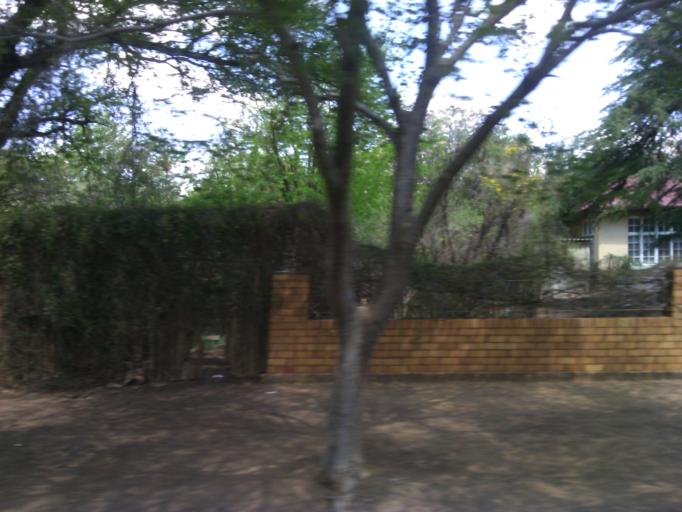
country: ZA
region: Orange Free State
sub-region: Xhariep District Municipality
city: Dewetsdorp
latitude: -29.5830
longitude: 26.6679
